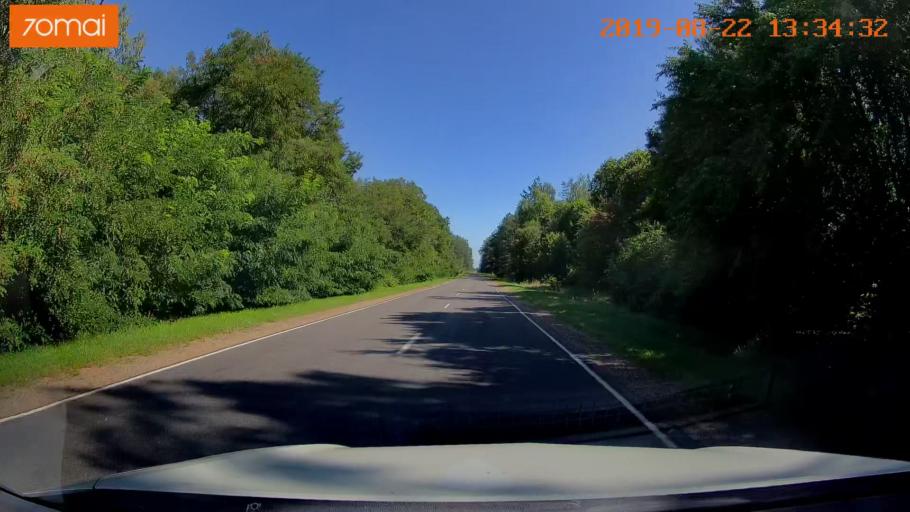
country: BY
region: Minsk
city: Staryya Darohi
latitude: 53.2151
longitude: 28.2441
